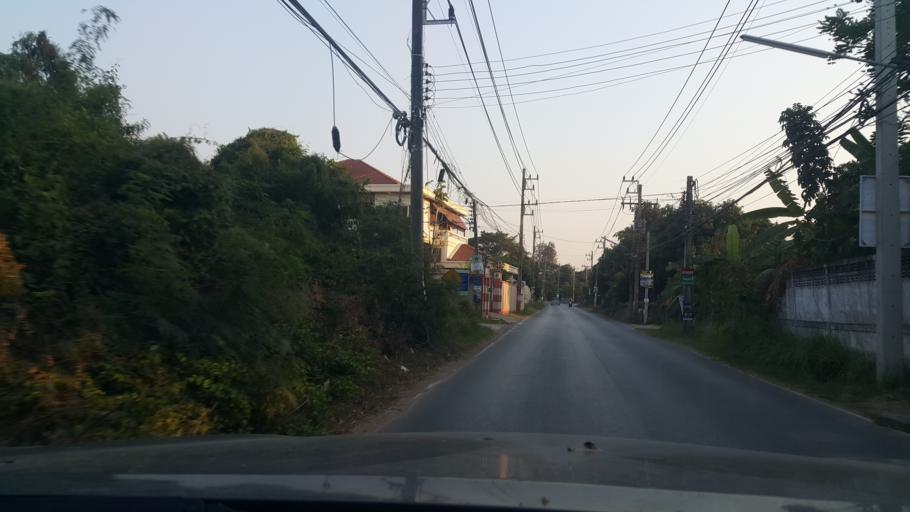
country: TH
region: Nakhon Ratchasima
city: Nakhon Ratchasima
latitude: 14.9443
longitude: 102.0287
